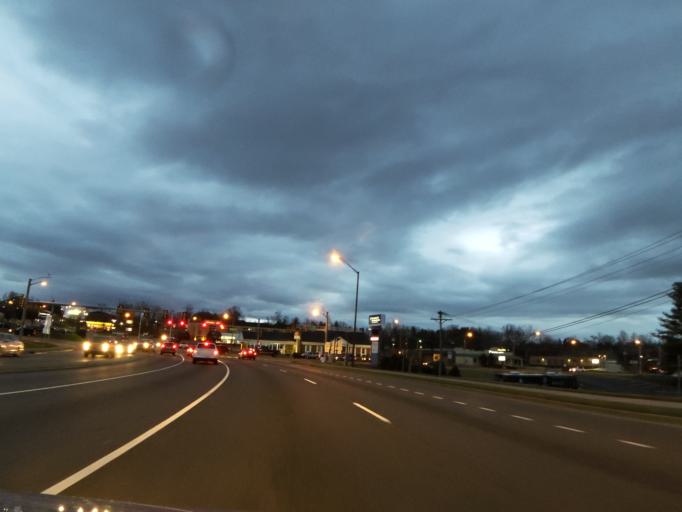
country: US
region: Tennessee
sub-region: Washington County
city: Johnson City
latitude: 36.3109
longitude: -82.3867
